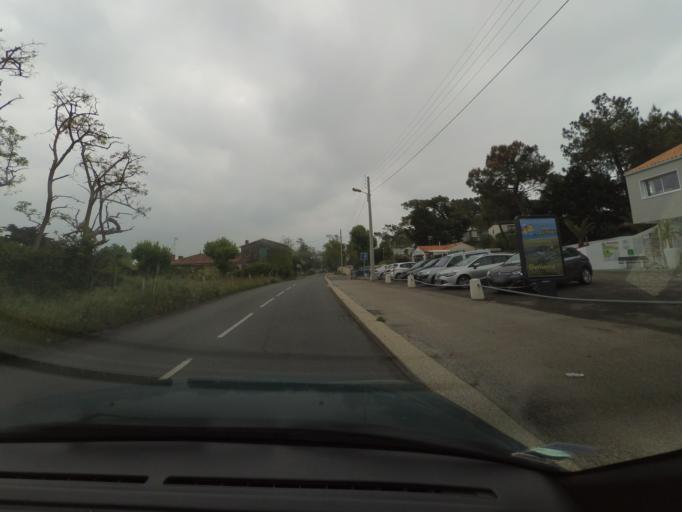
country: FR
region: Pays de la Loire
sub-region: Departement de la Vendee
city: Angles
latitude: 46.3489
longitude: -1.3615
